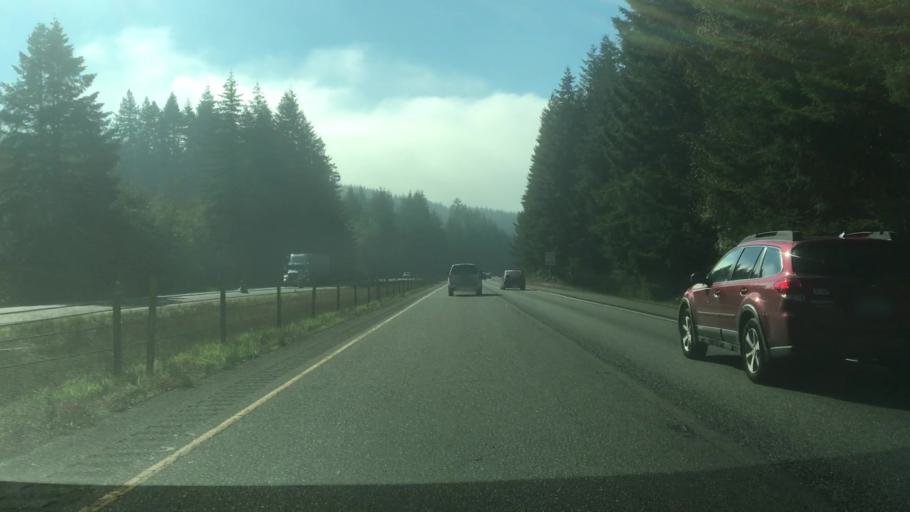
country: US
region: Washington
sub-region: Grays Harbor County
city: McCleary
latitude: 47.0438
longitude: -123.3166
